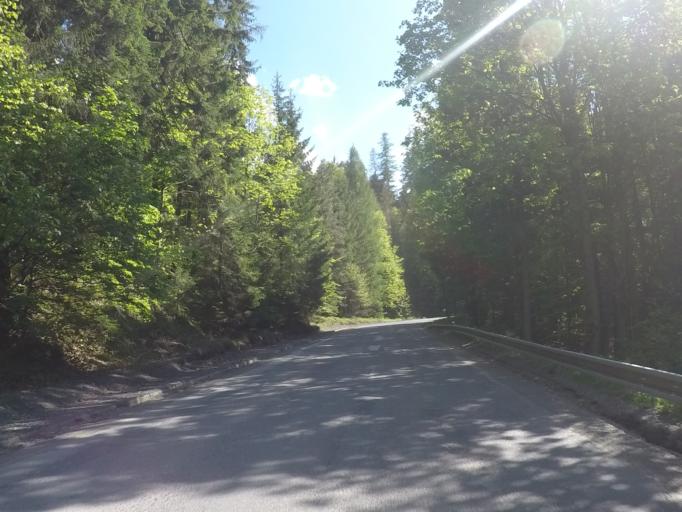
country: SK
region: Kosicky
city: Dobsina
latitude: 48.9125
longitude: 20.2607
